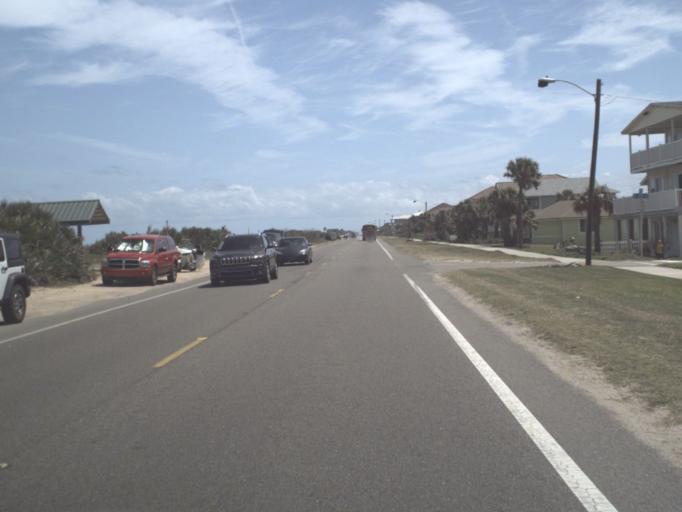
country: US
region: Florida
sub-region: Flagler County
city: Flagler Beach
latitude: 29.4930
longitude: -81.1334
